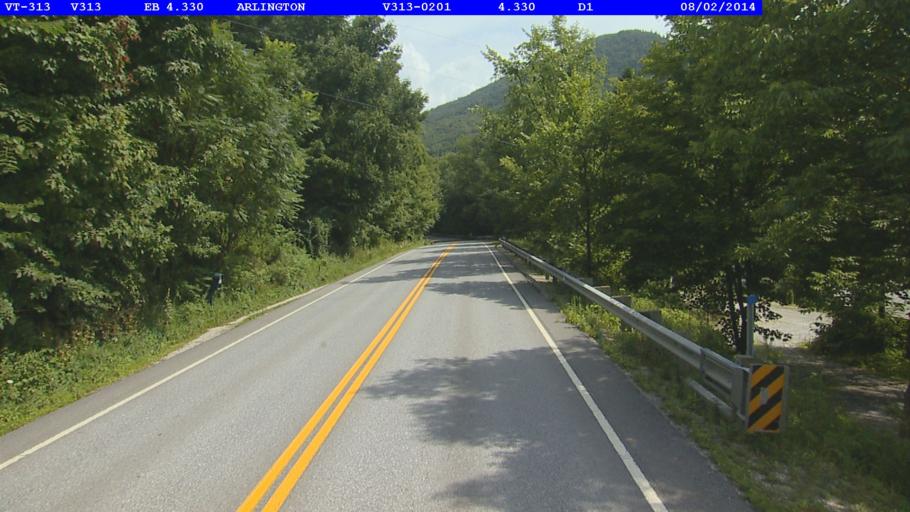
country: US
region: Vermont
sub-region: Bennington County
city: Arlington
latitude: 43.0873
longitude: -73.1933
